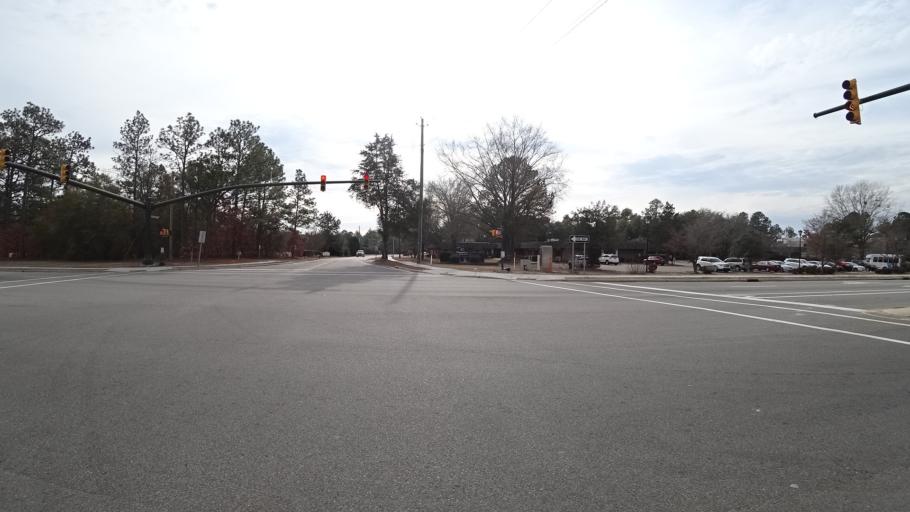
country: US
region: North Carolina
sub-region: Moore County
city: Pinehurst
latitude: 35.2065
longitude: -79.4652
